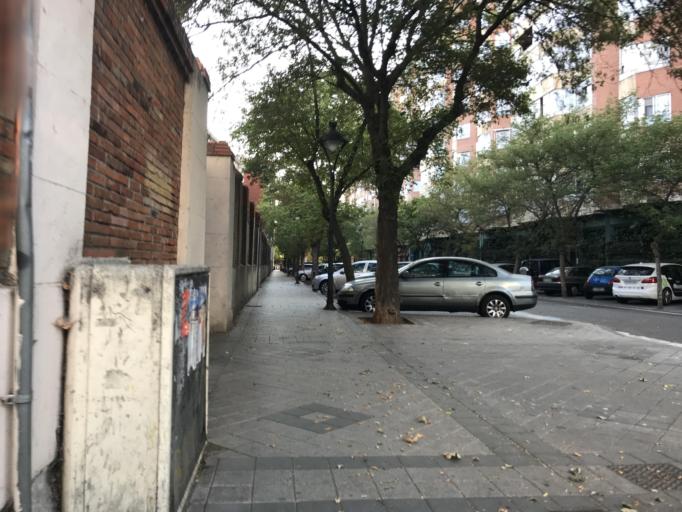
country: ES
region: Castille and Leon
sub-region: Provincia de Valladolid
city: Valladolid
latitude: 41.6497
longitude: -4.7195
